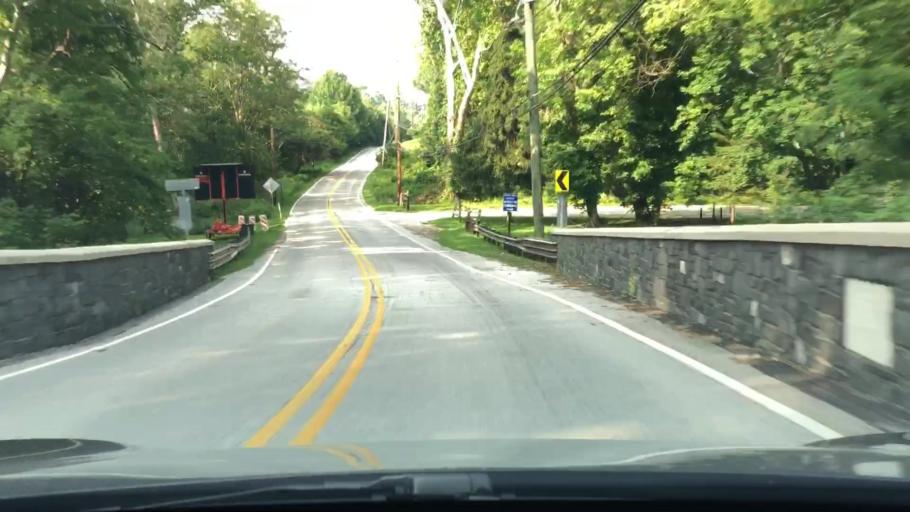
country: US
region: Pennsylvania
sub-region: Delaware County
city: Wayne
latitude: 40.0173
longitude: -75.4053
